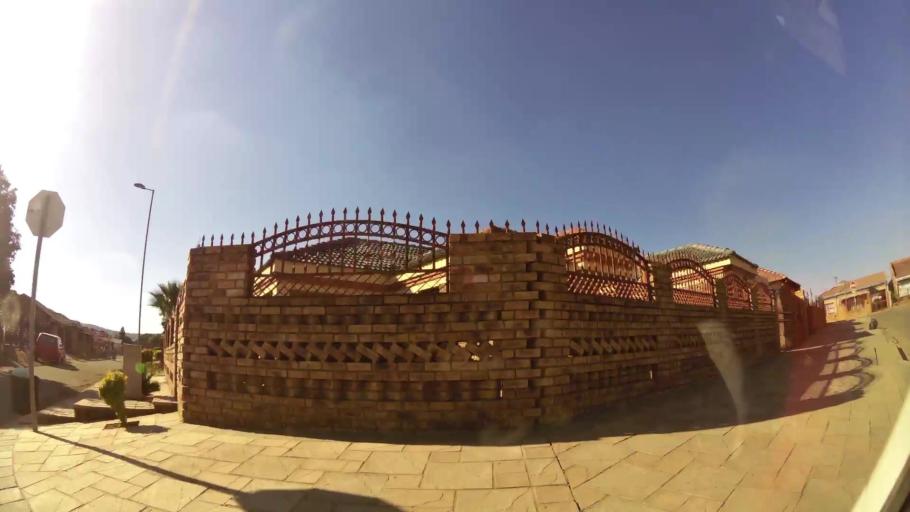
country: ZA
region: Gauteng
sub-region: City of Tshwane Metropolitan Municipality
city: Cullinan
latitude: -25.7197
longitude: 28.3797
